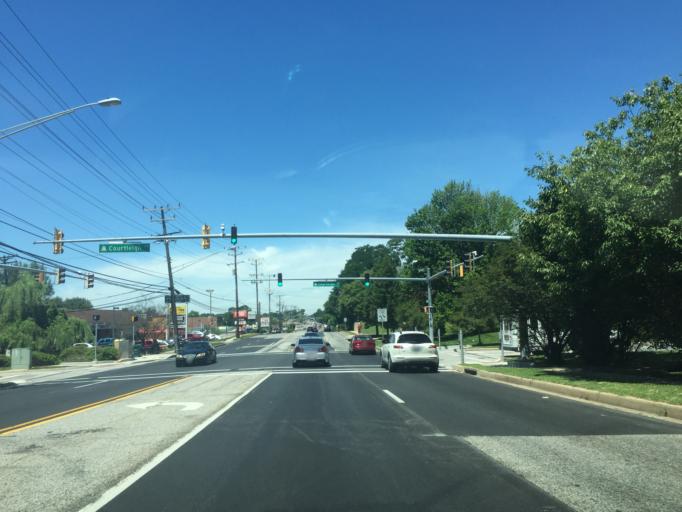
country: US
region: Maryland
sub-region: Baltimore County
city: Milford Mill
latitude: 39.3593
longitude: -76.7731
